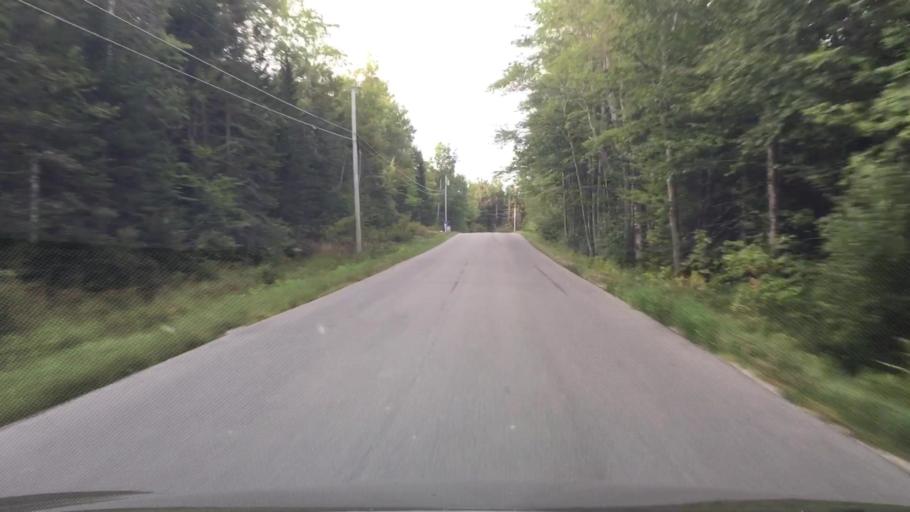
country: US
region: Maine
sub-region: Waldo County
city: Stockton Springs
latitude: 44.4962
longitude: -68.8742
